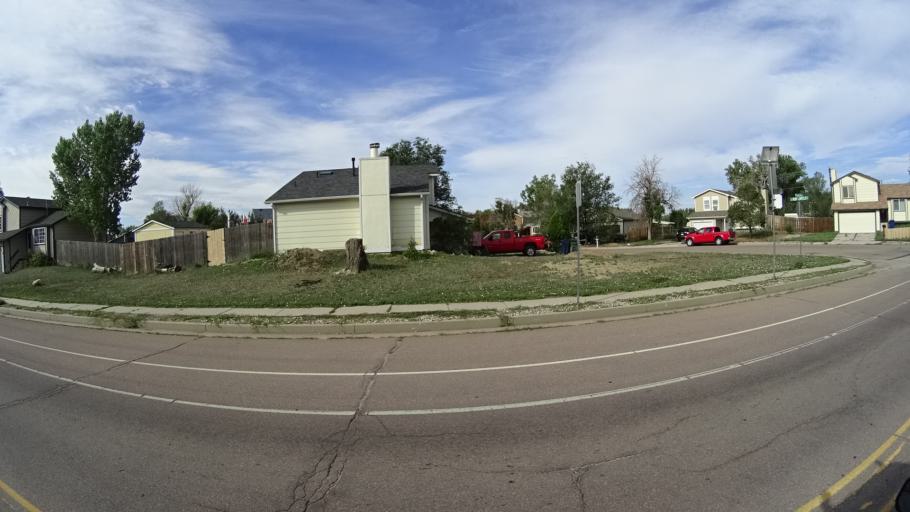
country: US
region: Colorado
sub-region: El Paso County
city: Fountain
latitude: 38.6926
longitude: -104.6959
